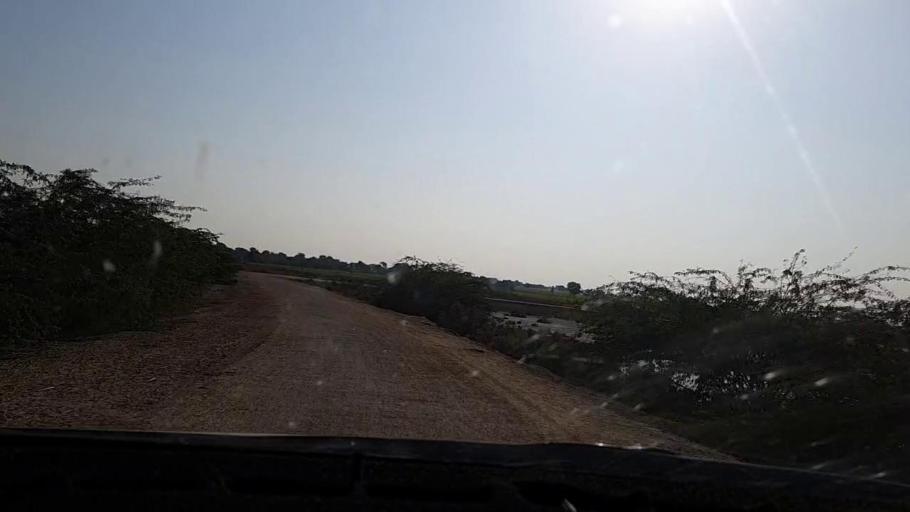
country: PK
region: Sindh
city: Tando Mittha Khan
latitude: 25.8314
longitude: 69.3205
